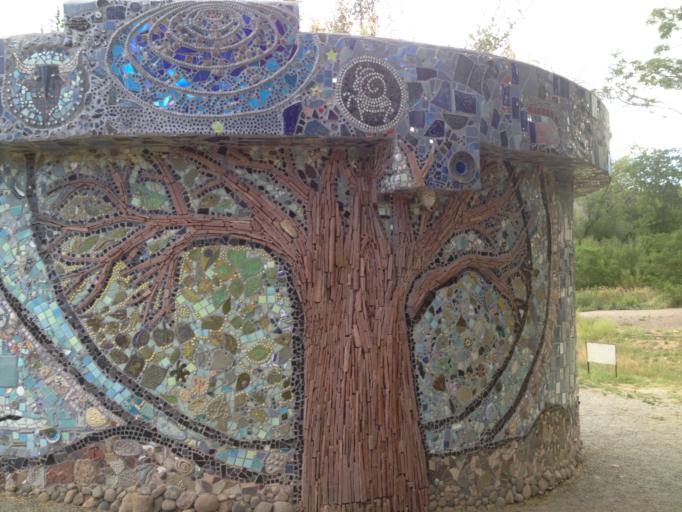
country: US
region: Colorado
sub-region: Boulder County
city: Lyons
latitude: 40.2202
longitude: -105.2634
